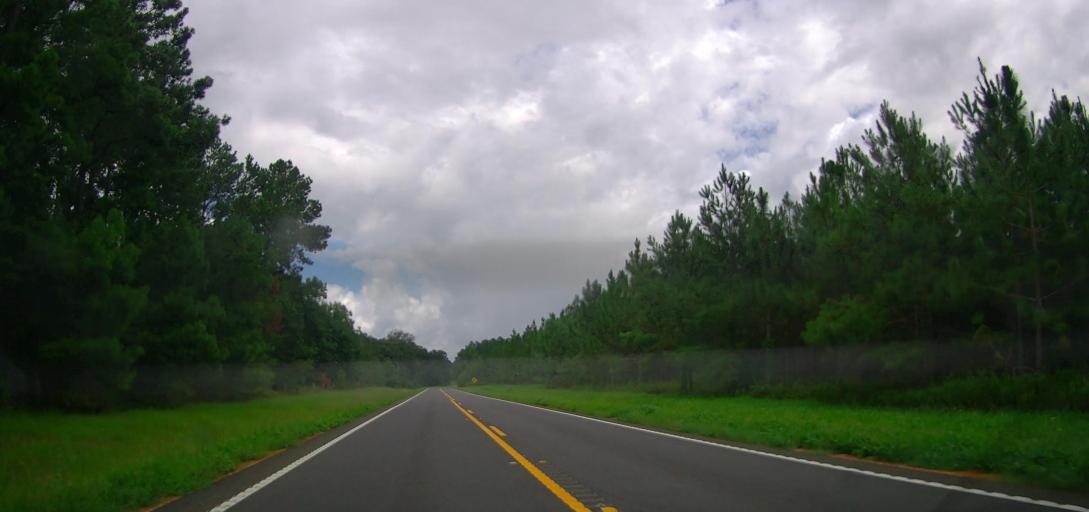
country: US
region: Georgia
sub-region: Pulaski County
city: Hawkinsville
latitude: 32.1351
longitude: -83.5599
